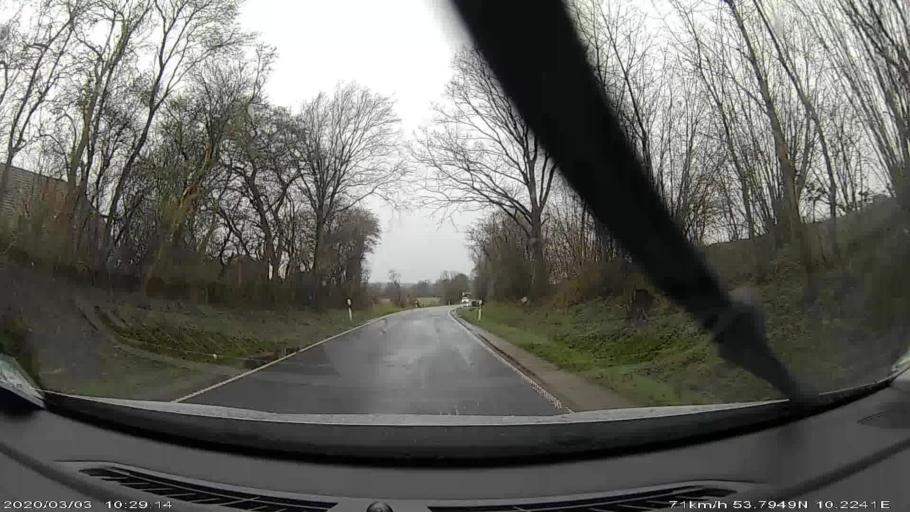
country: DE
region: Schleswig-Holstein
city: Sulfeld
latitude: 53.7975
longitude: 10.2274
